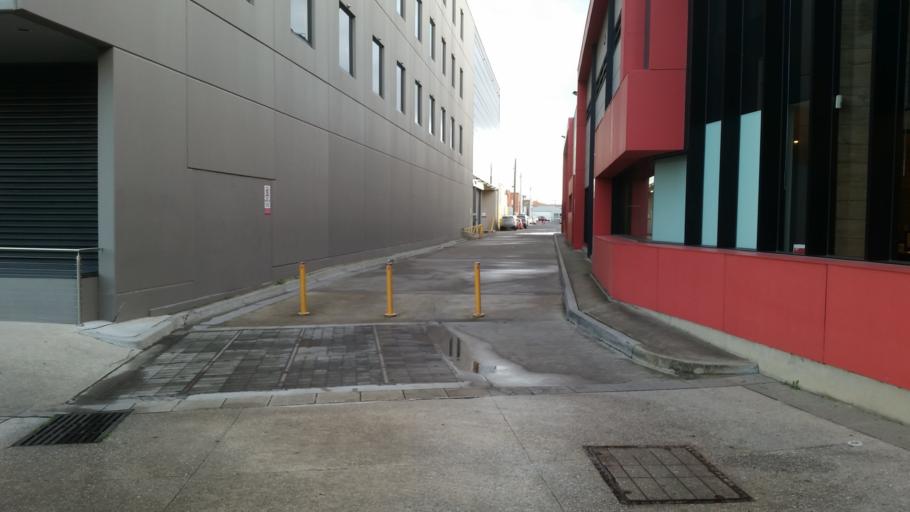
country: AU
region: Victoria
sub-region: Yarra
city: Richmond
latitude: -37.8134
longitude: 145.0120
